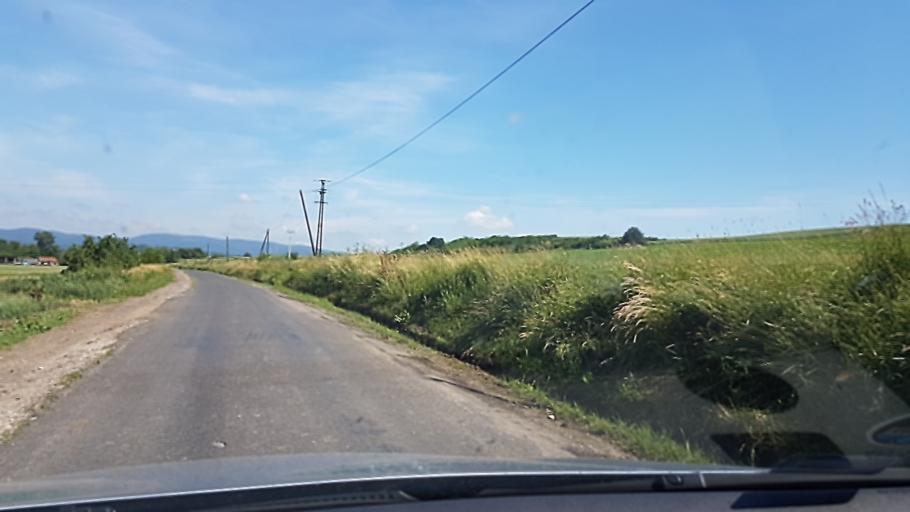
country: HU
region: Borsod-Abauj-Zemplen
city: Saly
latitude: 47.9478
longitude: 20.7016
